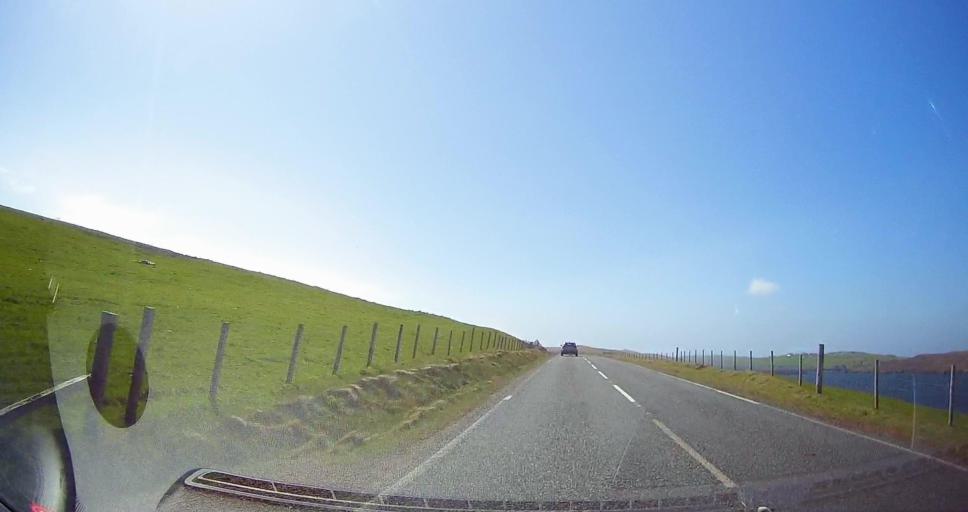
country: GB
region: Scotland
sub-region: Shetland Islands
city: Sandwick
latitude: 60.1139
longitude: -1.2944
